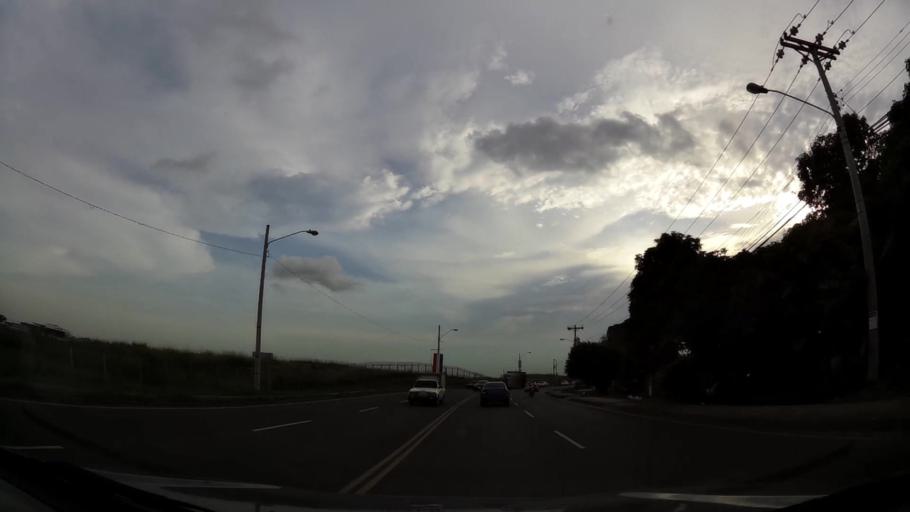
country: PA
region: Panama
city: Tocumen
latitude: 9.0945
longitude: -79.3765
